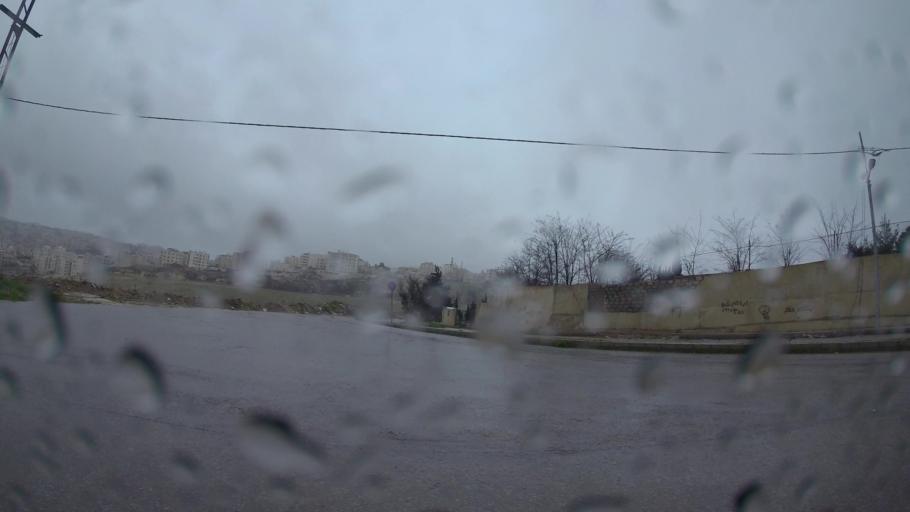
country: JO
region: Amman
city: Al Jubayhah
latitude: 32.0458
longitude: 35.8754
